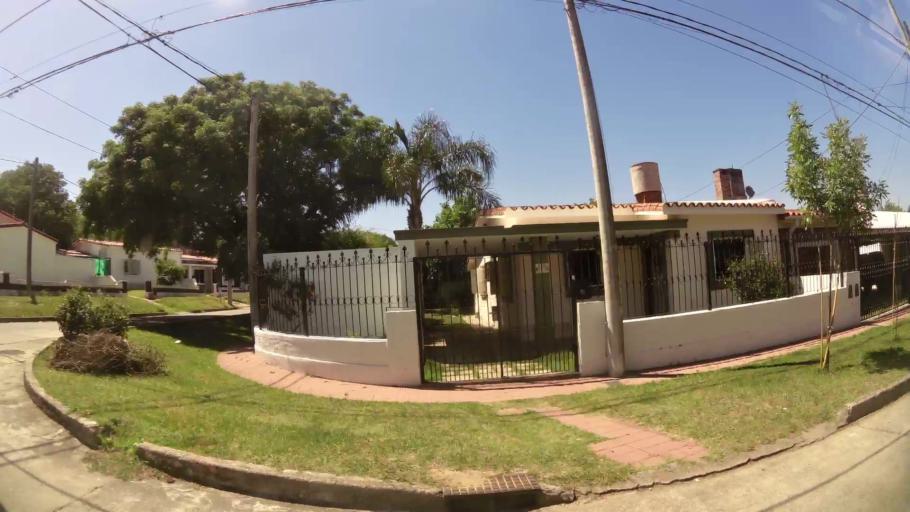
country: AR
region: Cordoba
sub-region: Departamento de Capital
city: Cordoba
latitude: -31.4325
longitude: -64.2107
